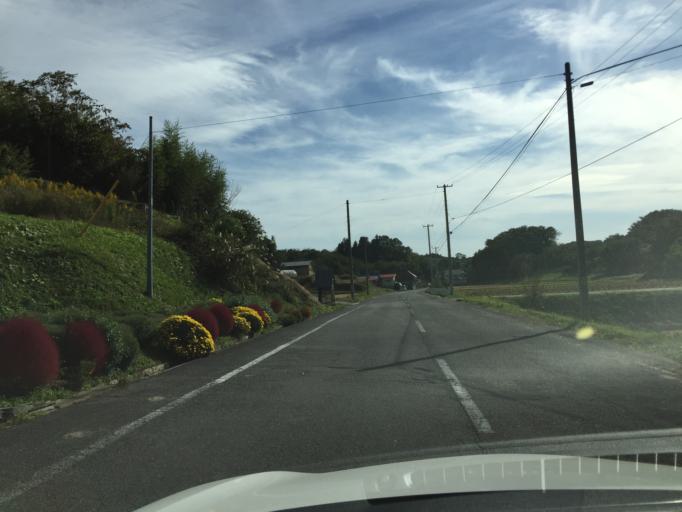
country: JP
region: Fukushima
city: Miharu
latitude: 37.4733
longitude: 140.4932
